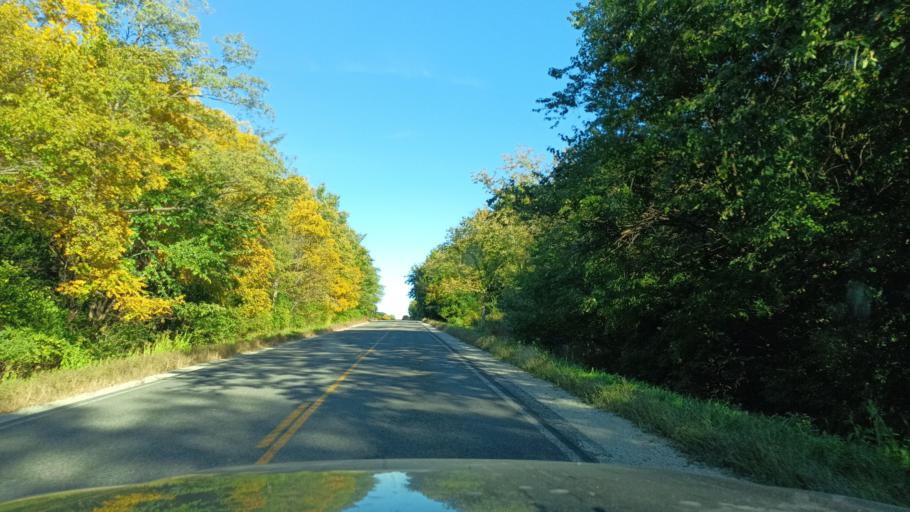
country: US
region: Illinois
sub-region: McLean County
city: Le Roy
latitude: 40.2245
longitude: -88.8185
